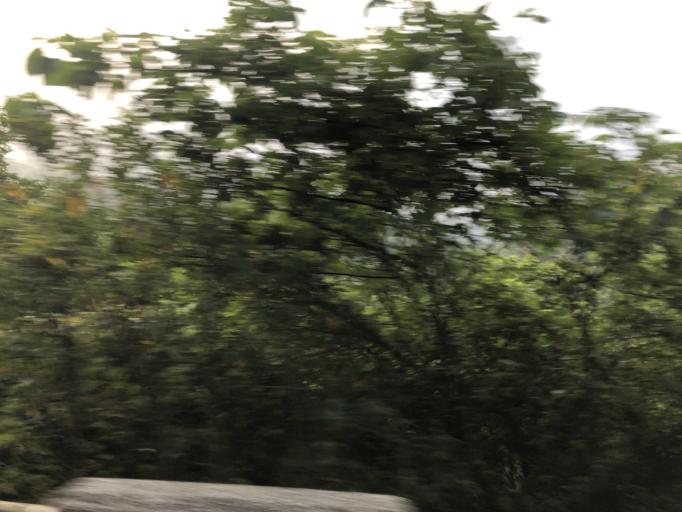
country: TW
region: Taiwan
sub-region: Keelung
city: Keelung
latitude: 25.1479
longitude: 121.6144
